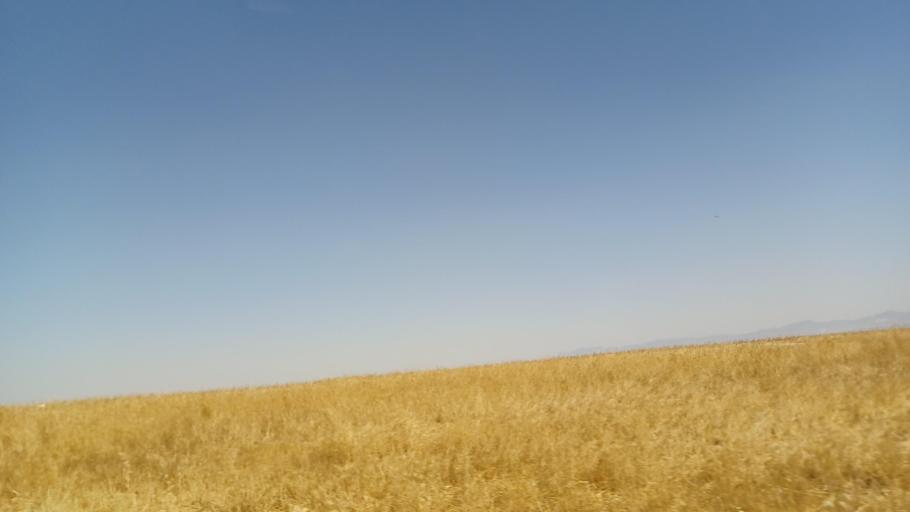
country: CY
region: Lefkosia
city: Lympia
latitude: 34.9763
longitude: 33.4828
